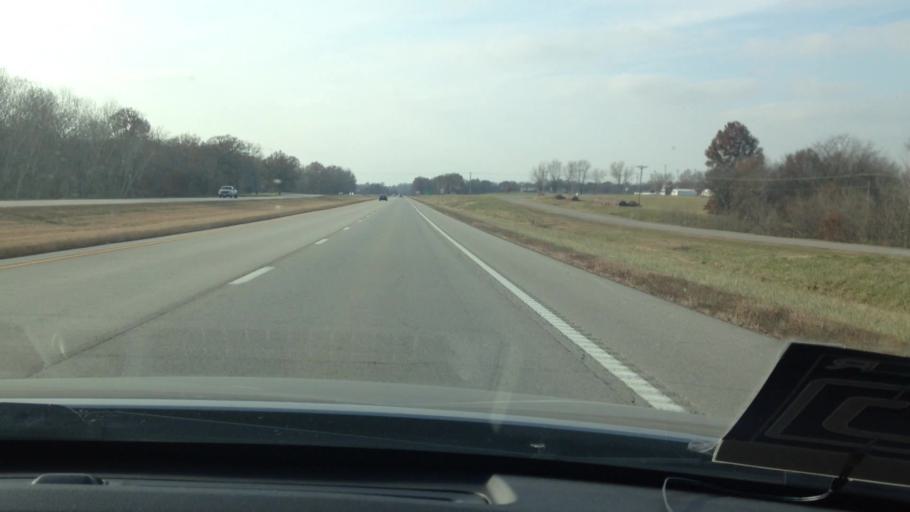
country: US
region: Missouri
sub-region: Cass County
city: Garden City
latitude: 38.5037
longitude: -94.0805
